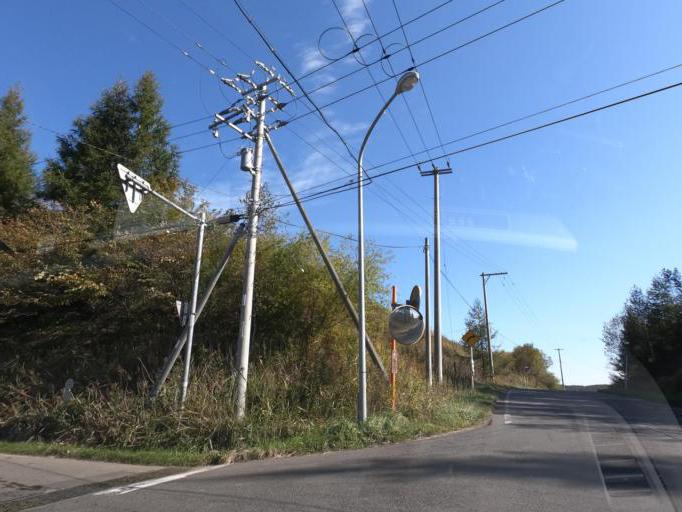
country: JP
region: Hokkaido
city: Otofuke
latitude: 42.9966
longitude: 143.2640
